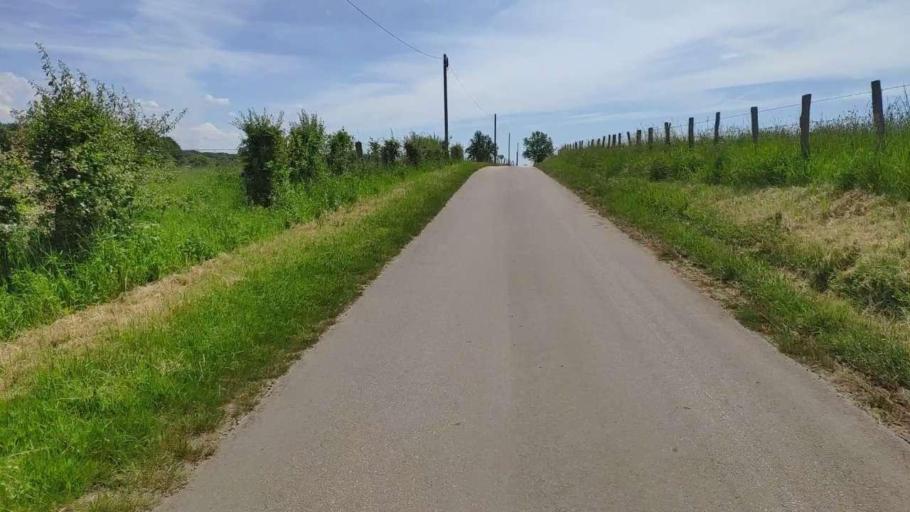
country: FR
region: Franche-Comte
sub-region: Departement du Jura
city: Bletterans
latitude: 46.7711
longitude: 5.4321
